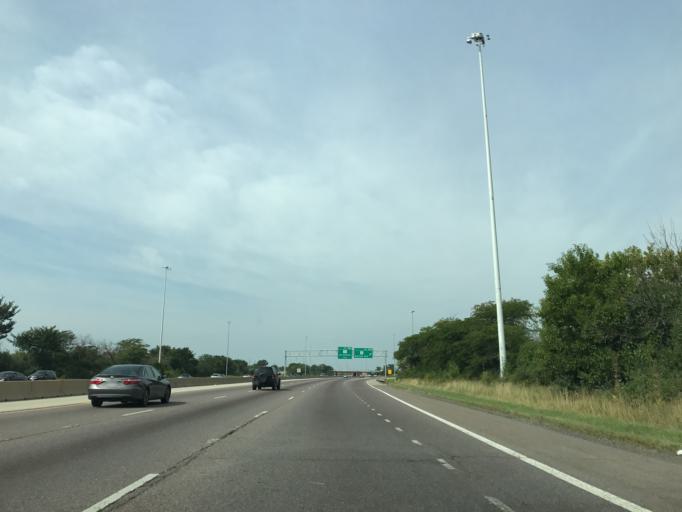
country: US
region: Illinois
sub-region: Cook County
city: Summit
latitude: 41.8015
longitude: -87.7932
